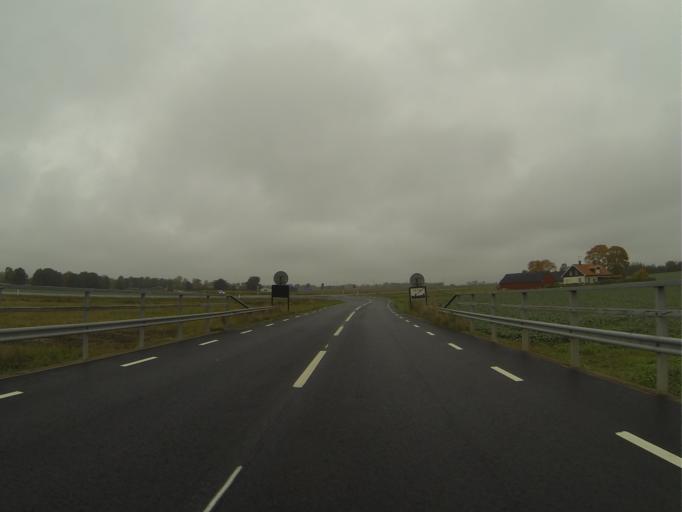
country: SE
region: Skane
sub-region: Tomelilla Kommun
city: Tomelilla
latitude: 55.5721
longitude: 13.9286
